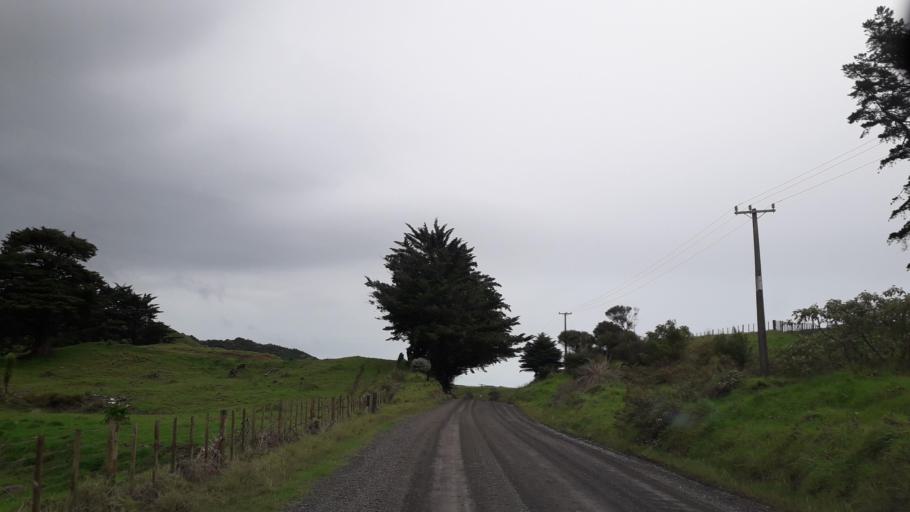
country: NZ
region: Northland
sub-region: Far North District
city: Ahipara
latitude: -35.4187
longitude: 173.3624
